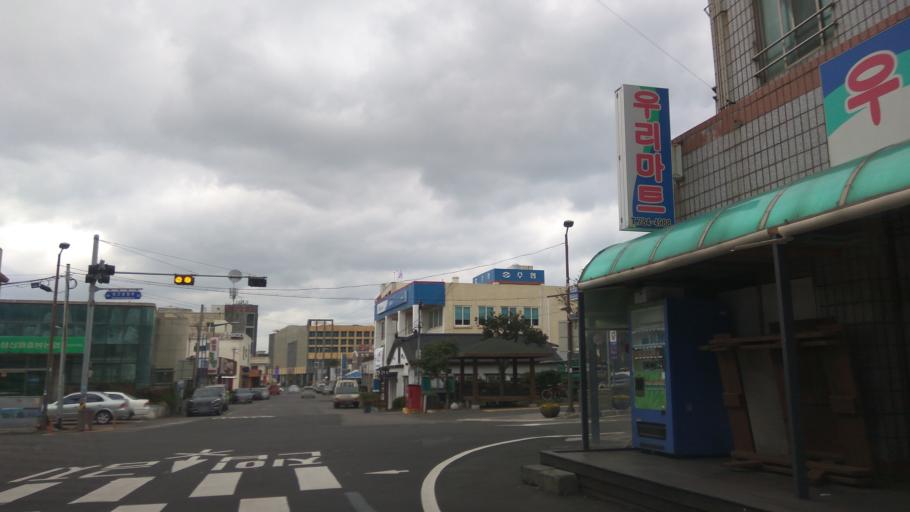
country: KR
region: Jeju-do
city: Jeju-si
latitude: 33.4640
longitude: 126.9343
